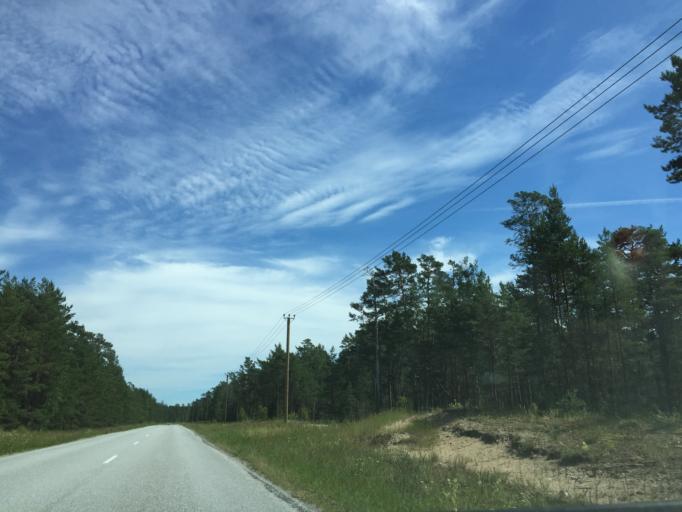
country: LV
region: Rojas
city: Roja
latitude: 57.5731
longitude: 22.6361
